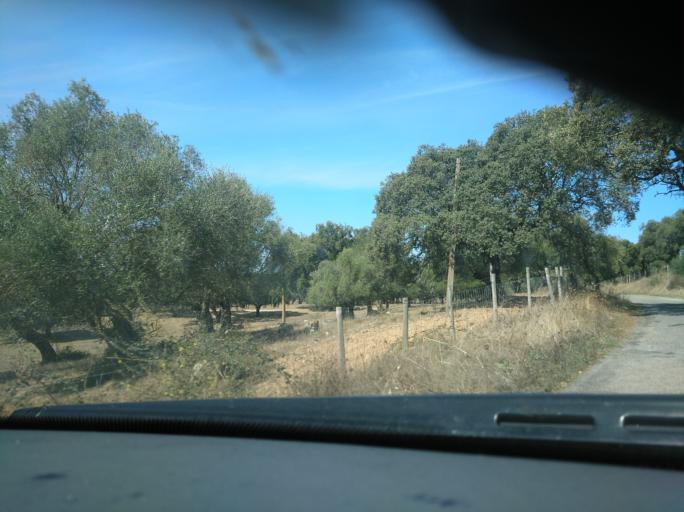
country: PT
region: Evora
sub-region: Arraiolos
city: Arraiolos
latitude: 38.6970
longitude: -8.0937
